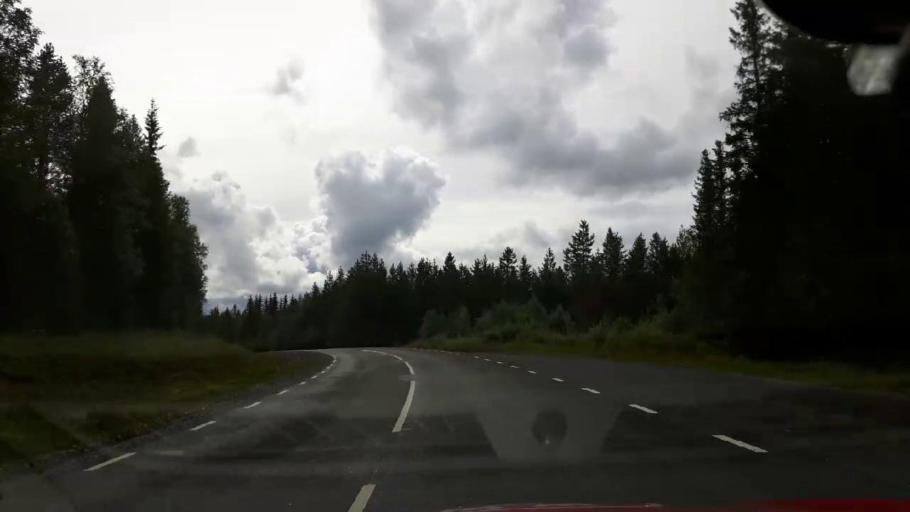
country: NO
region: Nord-Trondelag
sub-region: Lierne
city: Sandvika
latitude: 64.6393
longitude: 14.1364
